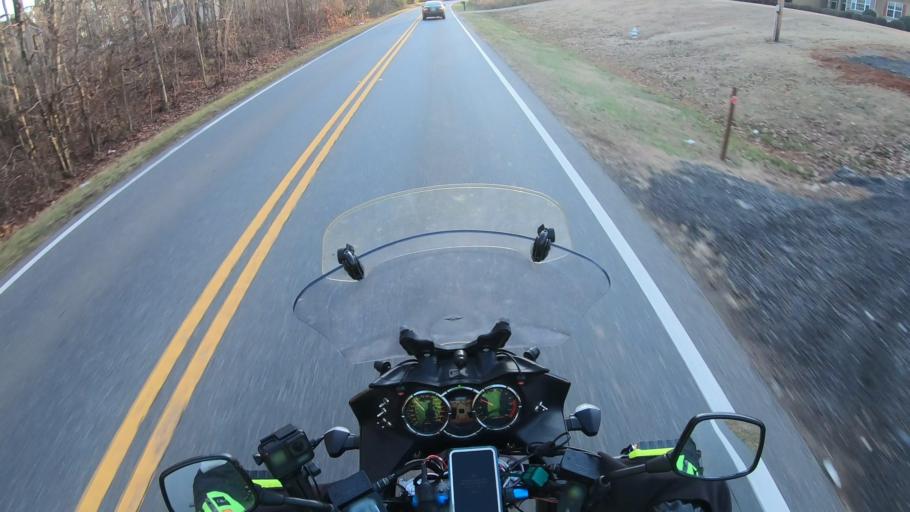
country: US
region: Georgia
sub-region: Dawson County
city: Dawsonville
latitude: 34.3250
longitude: -84.1316
